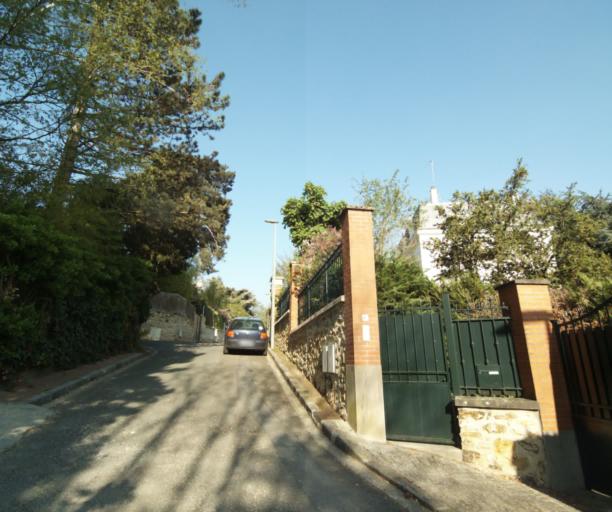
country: FR
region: Ile-de-France
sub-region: Departement des Hauts-de-Seine
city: Ville-d'Avray
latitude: 48.8288
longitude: 2.2032
